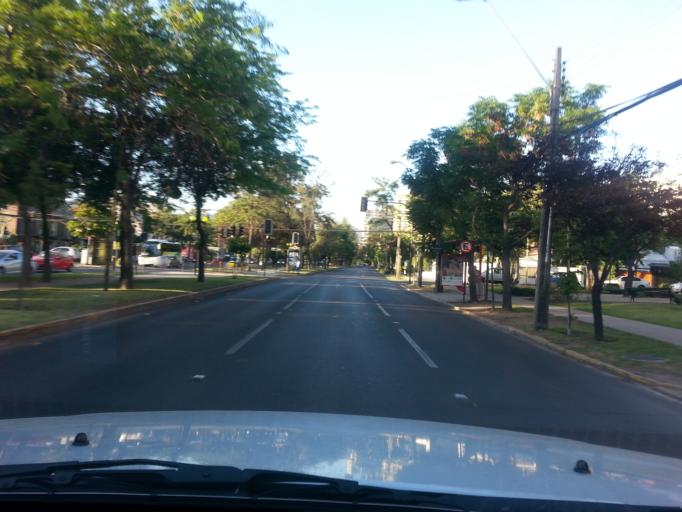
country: CL
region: Santiago Metropolitan
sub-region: Provincia de Santiago
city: Villa Presidente Frei, Nunoa, Santiago, Chile
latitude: -33.4212
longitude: -70.5642
